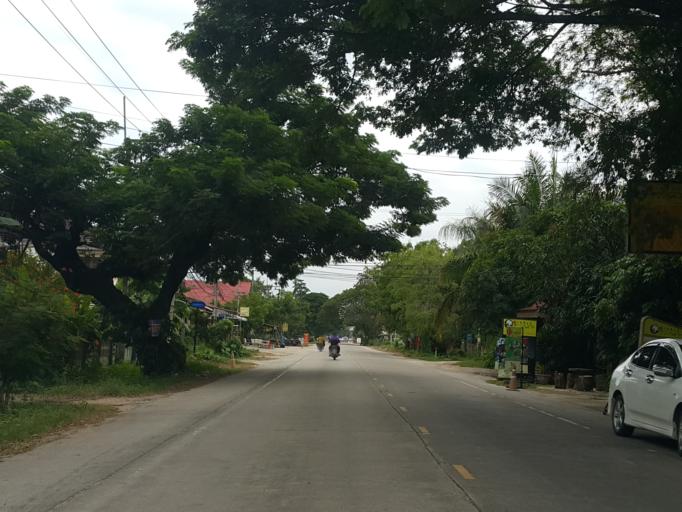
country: TH
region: Lampang
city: Lampang
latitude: 18.3068
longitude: 99.4965
